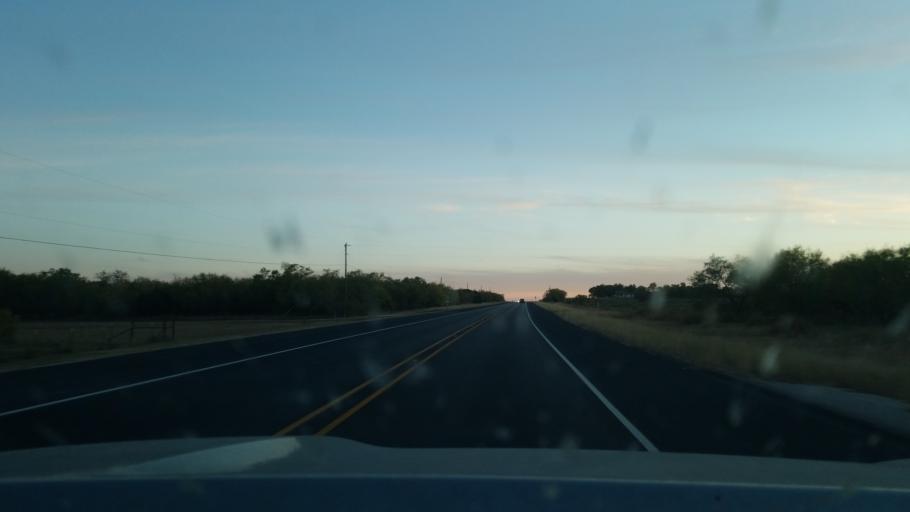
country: US
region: Texas
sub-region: Stephens County
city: Breckenridge
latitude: 32.6096
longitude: -98.8992
